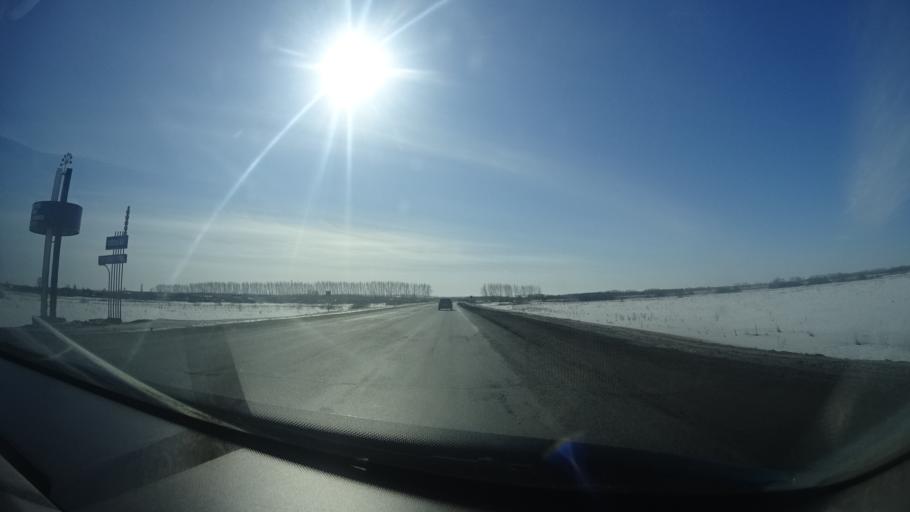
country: RU
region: Bashkortostan
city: Mikhaylovka
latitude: 54.9281
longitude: 55.7404
